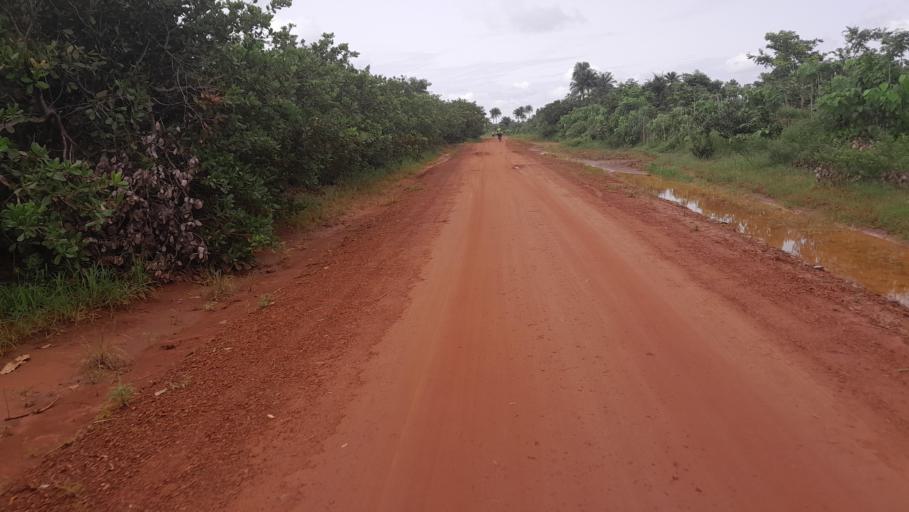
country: GN
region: Boke
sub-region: Boffa
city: Boffa
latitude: 10.0645
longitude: -13.8680
